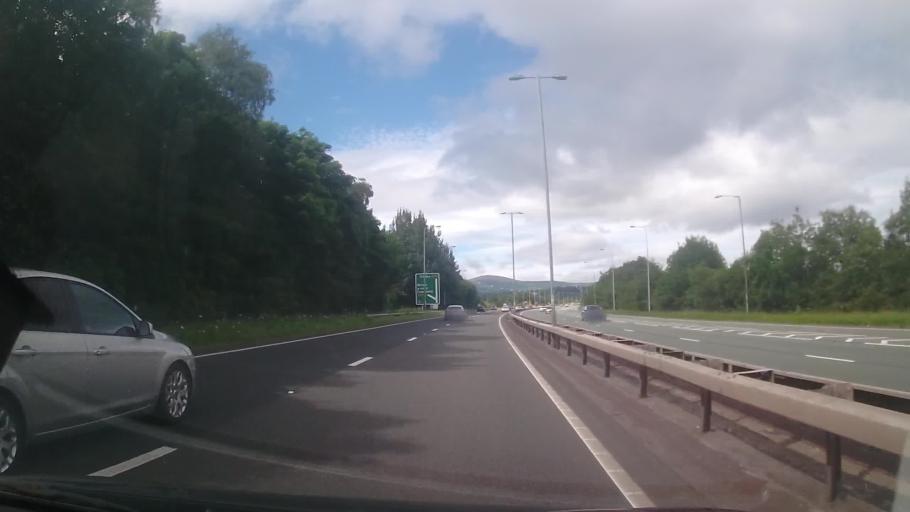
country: GB
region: Wales
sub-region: Conwy
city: Llansantffraid Glan Conwy
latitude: 53.2826
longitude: -3.7810
